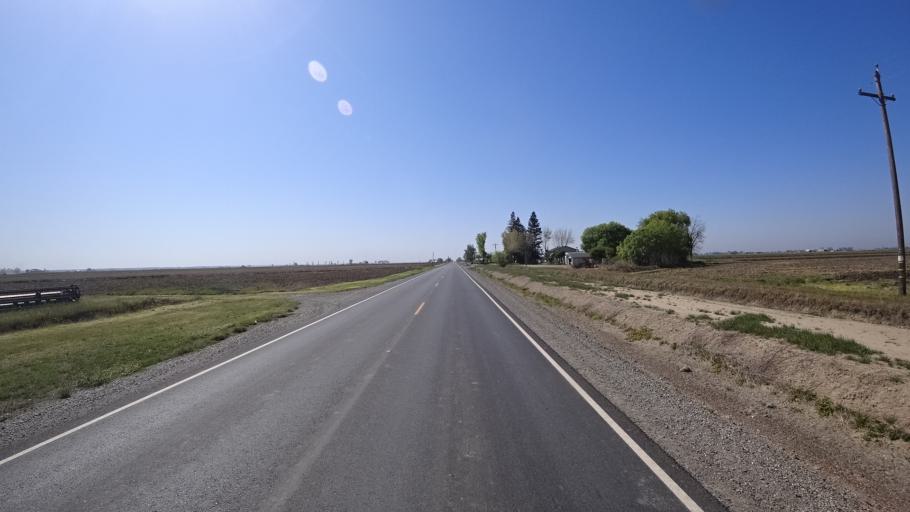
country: US
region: California
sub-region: Glenn County
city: Willows
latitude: 39.5807
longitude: -122.0652
